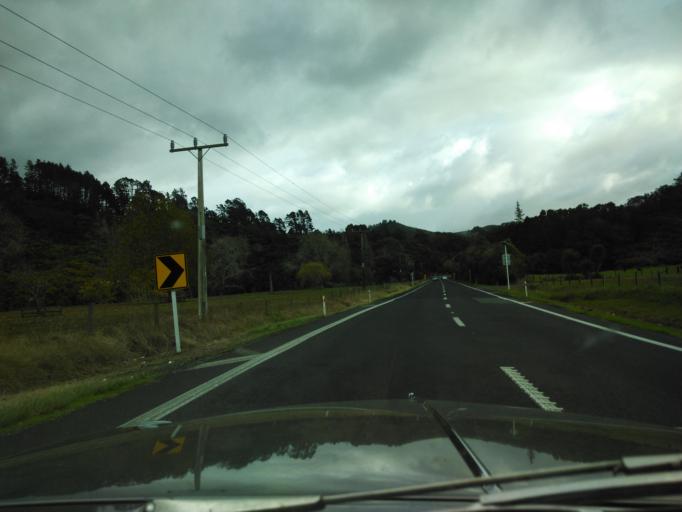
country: NZ
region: Waikato
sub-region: Hauraki District
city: Waihi
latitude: -37.4194
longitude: 175.7523
